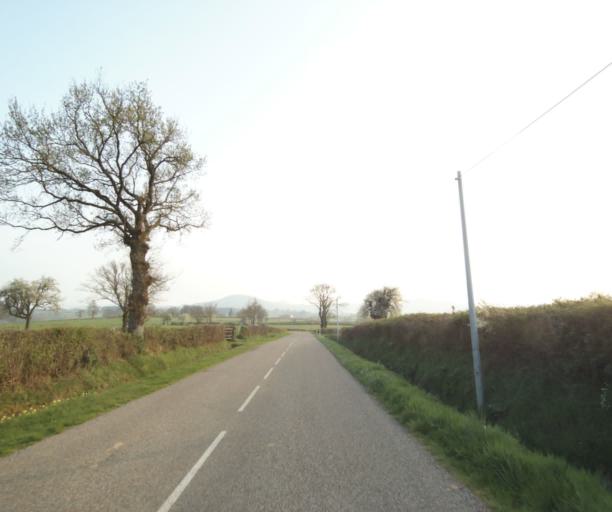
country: FR
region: Bourgogne
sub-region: Departement de Saone-et-Loire
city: Charolles
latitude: 46.4472
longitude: 4.4276
